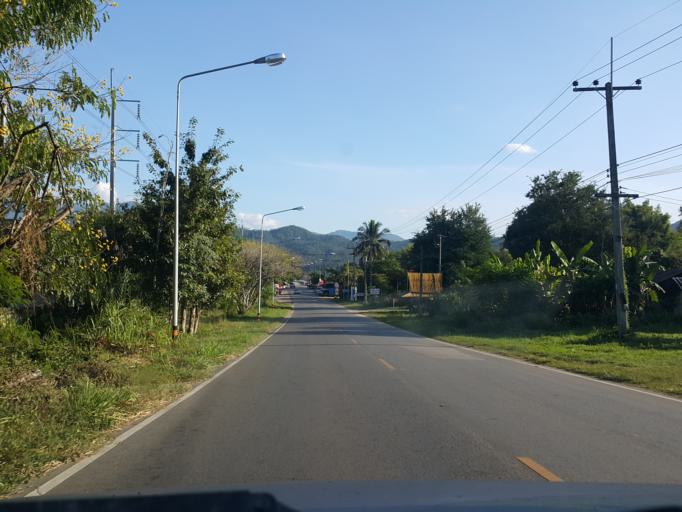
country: TH
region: Mae Hong Son
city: Mae Hi
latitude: 19.3011
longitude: 98.4628
